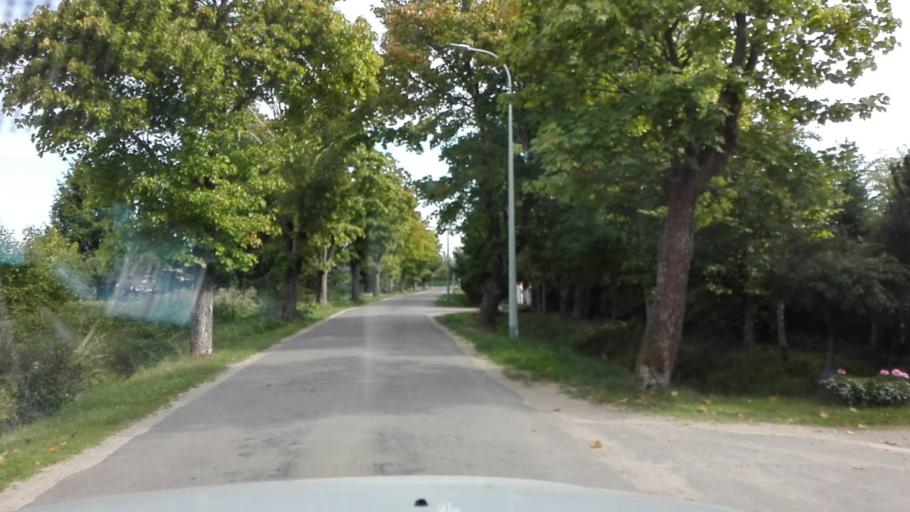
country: PL
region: West Pomeranian Voivodeship
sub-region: Powiat slawienski
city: Slawno
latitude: 54.5309
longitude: 16.5879
